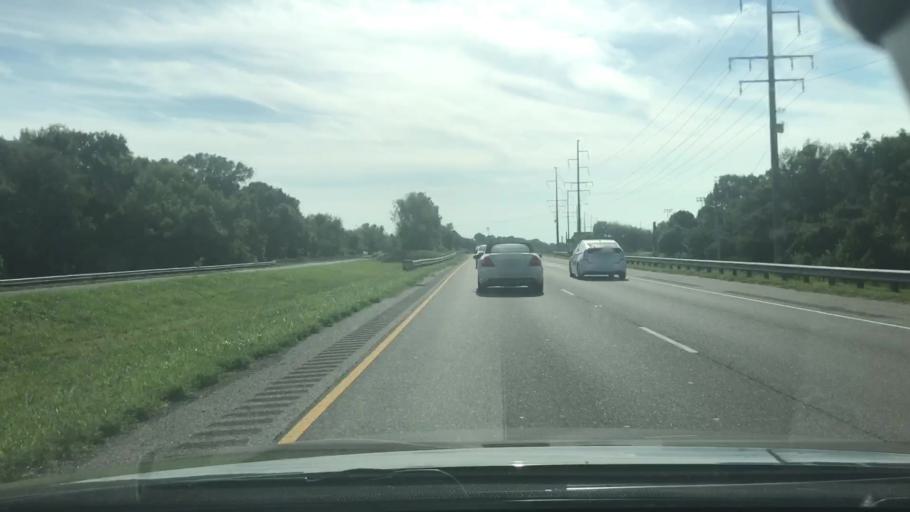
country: US
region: Tennessee
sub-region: Williamson County
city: Franklin
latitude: 35.9466
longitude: -86.8697
